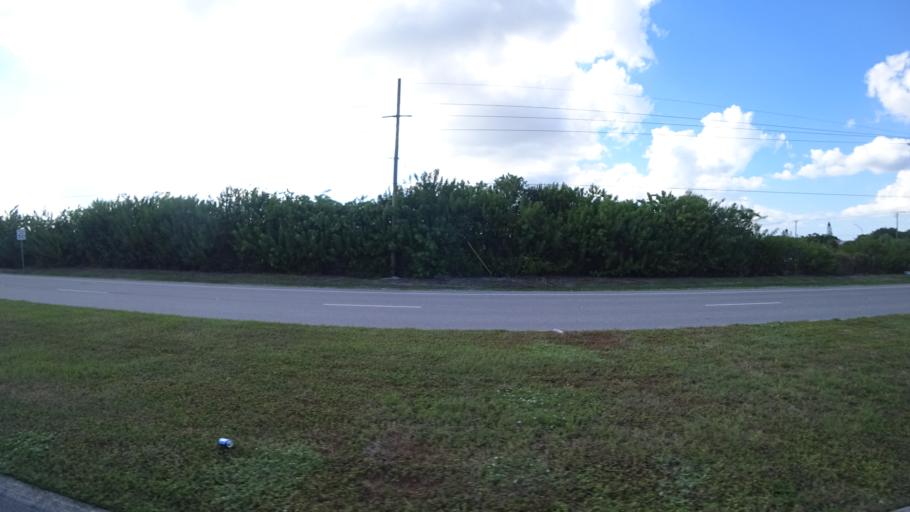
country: US
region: Florida
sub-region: Manatee County
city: West Bradenton
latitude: 27.4609
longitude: -82.6369
